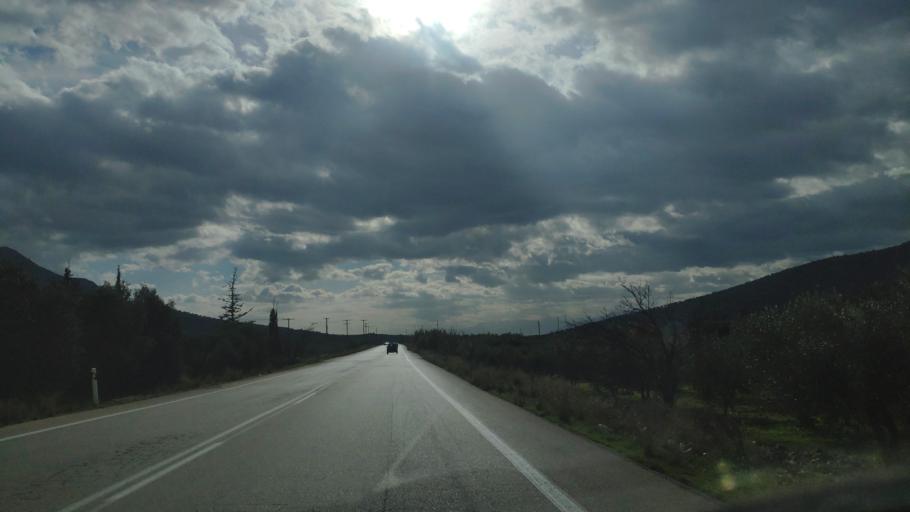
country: GR
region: Peloponnese
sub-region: Nomos Argolidos
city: Koutsopodi
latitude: 37.7504
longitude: 22.7353
